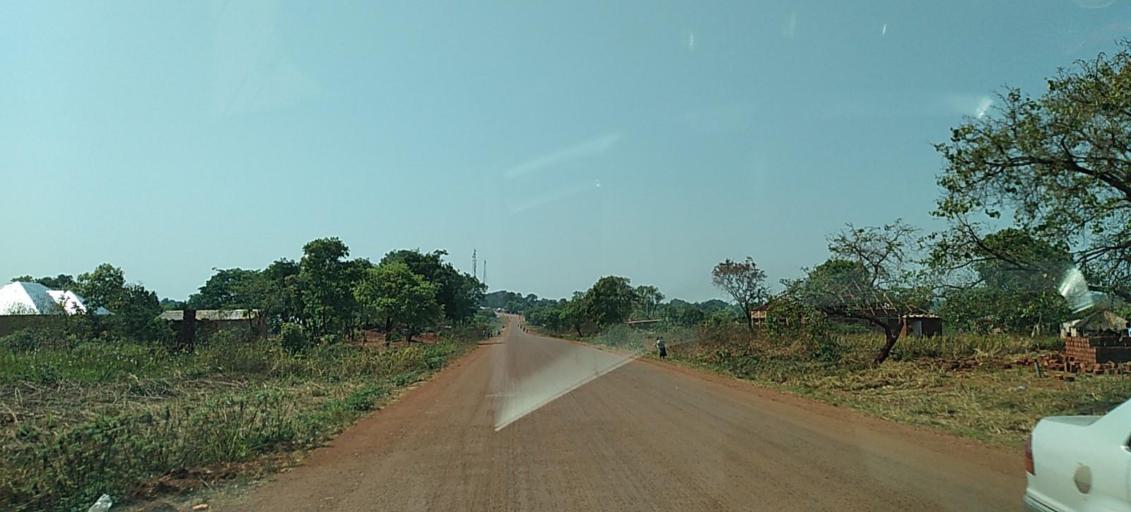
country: ZM
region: North-Western
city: Solwezi
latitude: -12.1021
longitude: 25.4922
